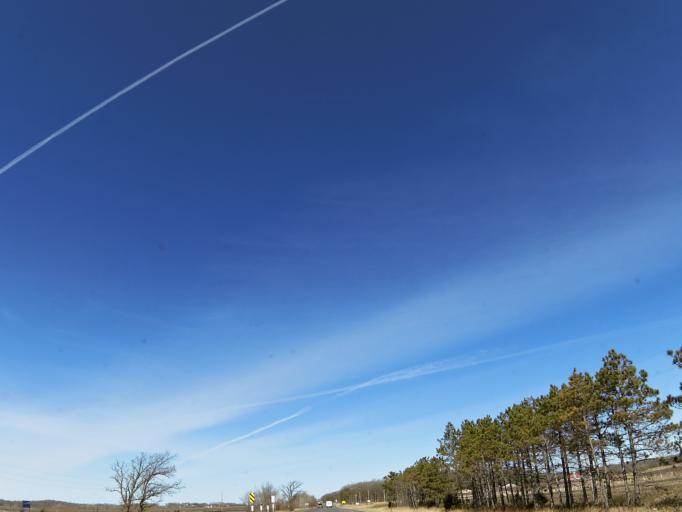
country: US
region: Minnesota
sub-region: Wright County
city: Buffalo
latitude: 45.1209
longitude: -93.8133
